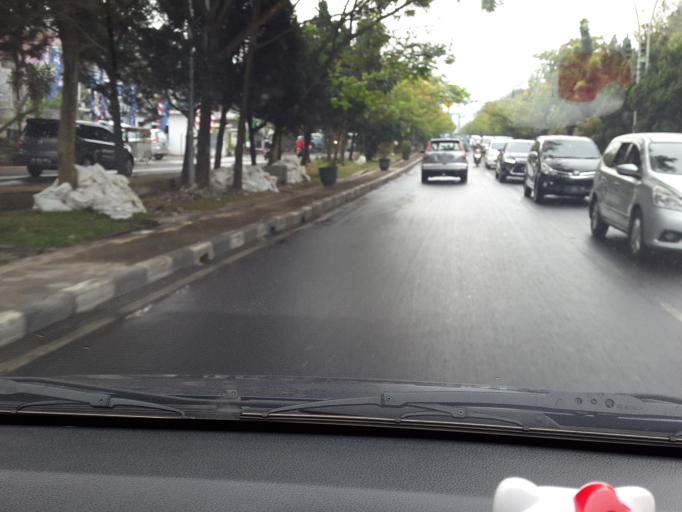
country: ID
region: West Java
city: Bandung
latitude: -6.8974
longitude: 107.6343
